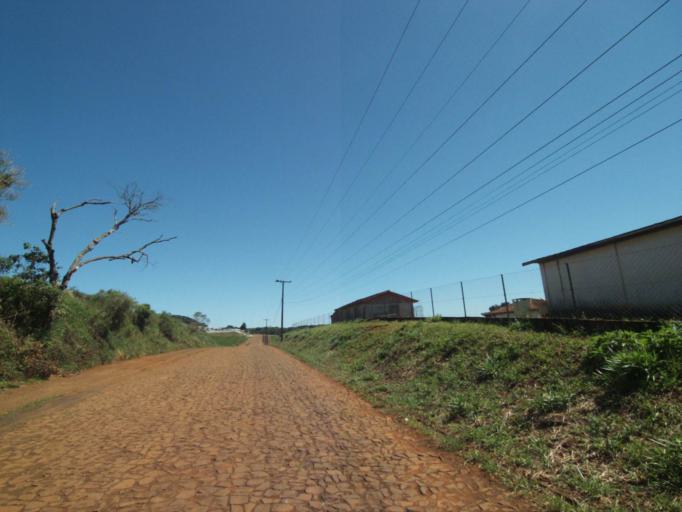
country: BR
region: Parana
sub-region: Pato Branco
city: Pato Branco
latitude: -26.2609
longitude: -52.7821
